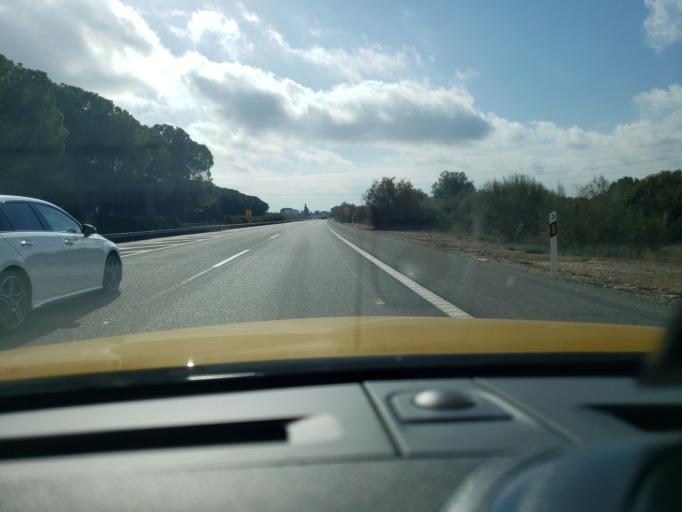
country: ES
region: Andalusia
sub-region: Provincia de Sevilla
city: Dos Hermanas
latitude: 37.2400
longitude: -5.9111
